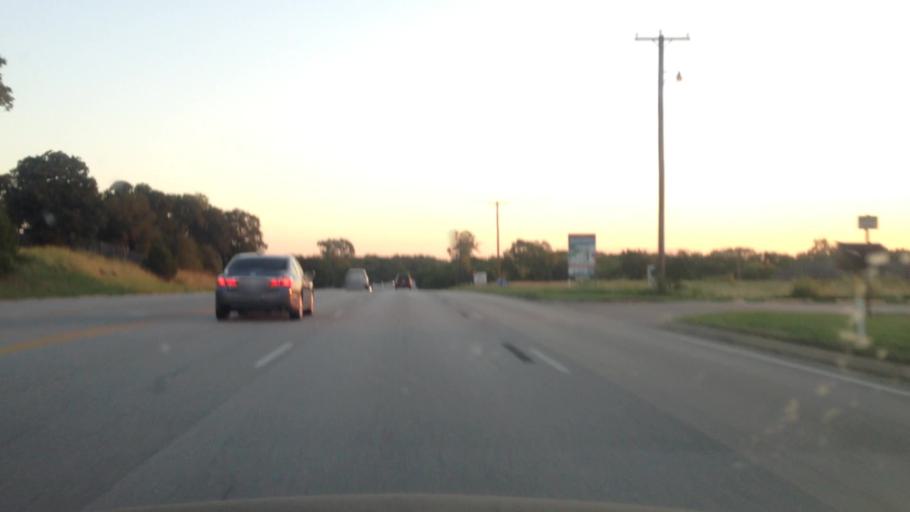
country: US
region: Texas
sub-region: Tarrant County
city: North Richland Hills
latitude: 32.8709
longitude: -97.2079
